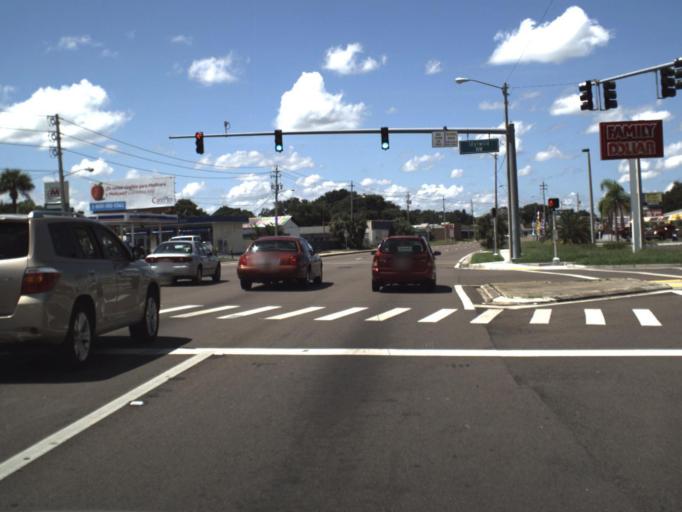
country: US
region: Florida
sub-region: Polk County
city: Inwood
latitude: 28.0464
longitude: -81.7595
